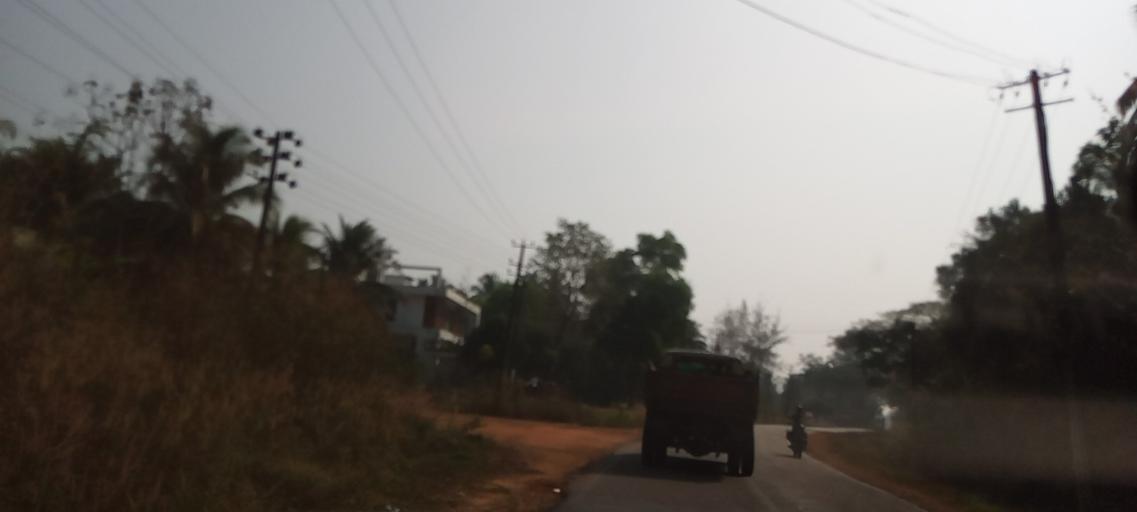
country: IN
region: Karnataka
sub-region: Udupi
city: Coondapoor
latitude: 13.5163
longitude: 74.7454
